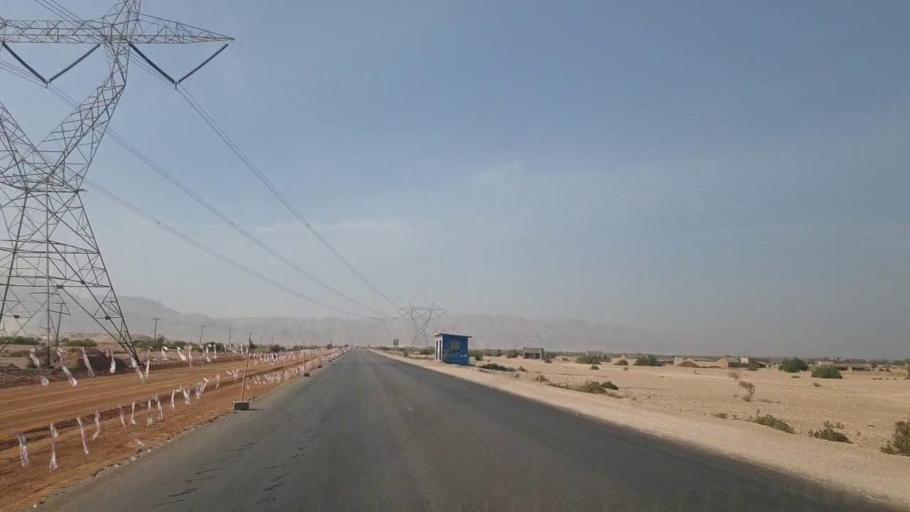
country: PK
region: Sindh
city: Sehwan
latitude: 26.2090
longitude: 67.9259
